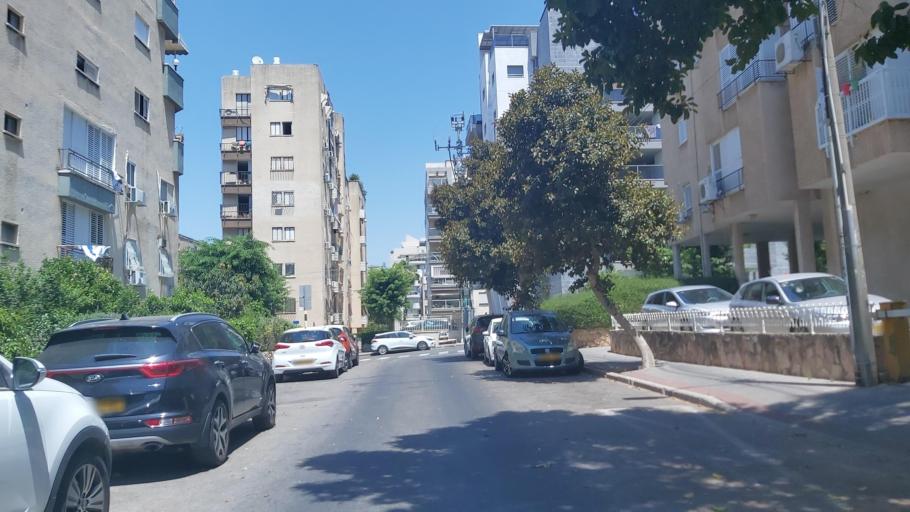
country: IL
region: Central District
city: Rishon LeZiyyon
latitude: 31.9626
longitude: 34.8089
